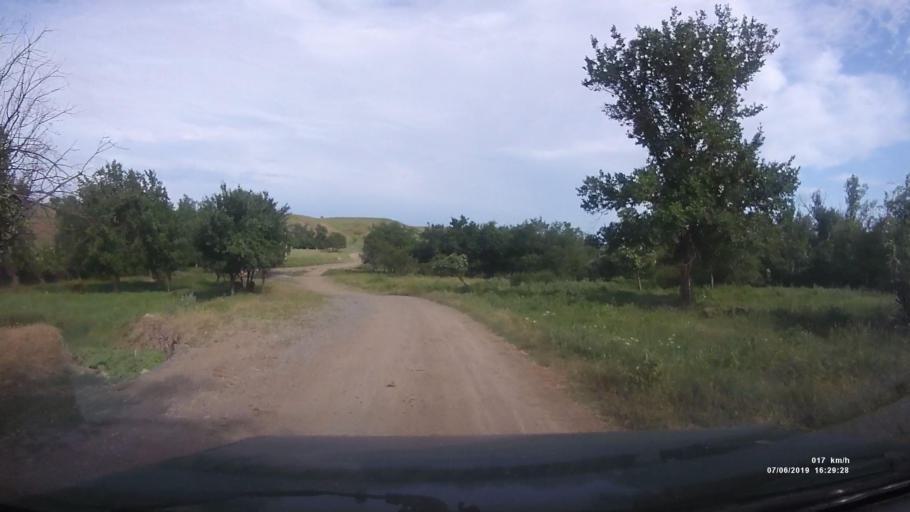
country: RU
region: Rostov
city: Staraya Stanitsa
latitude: 48.2551
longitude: 40.3208
